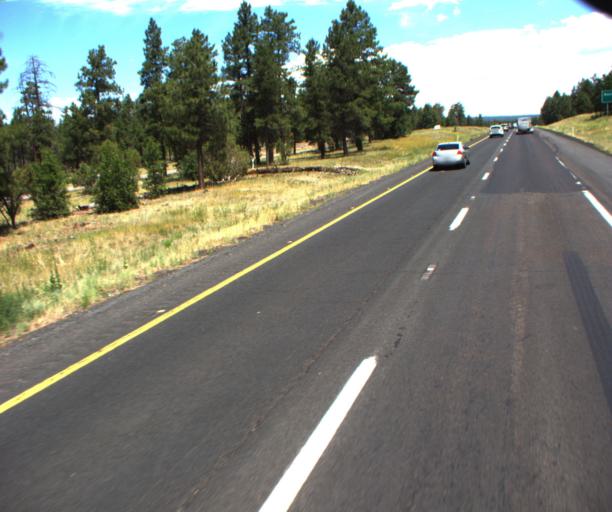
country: US
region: Arizona
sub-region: Coconino County
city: Sedona
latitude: 34.8350
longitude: -111.6048
